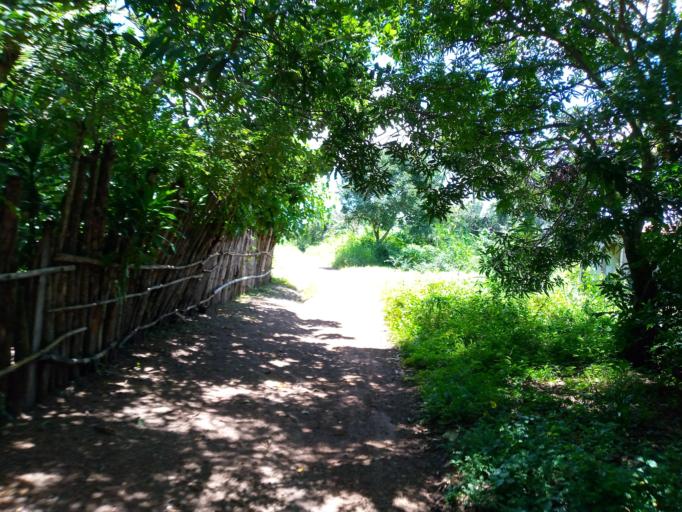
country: SL
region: Northern Province
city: Makeni
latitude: 9.0325
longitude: -12.1633
